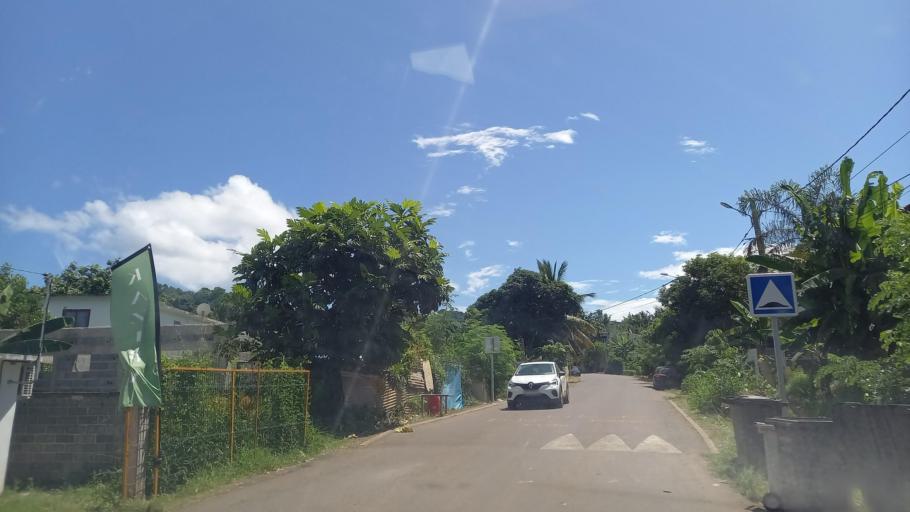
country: YT
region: Kani-Keli
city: Kani Keli
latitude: -12.9250
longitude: 45.1036
